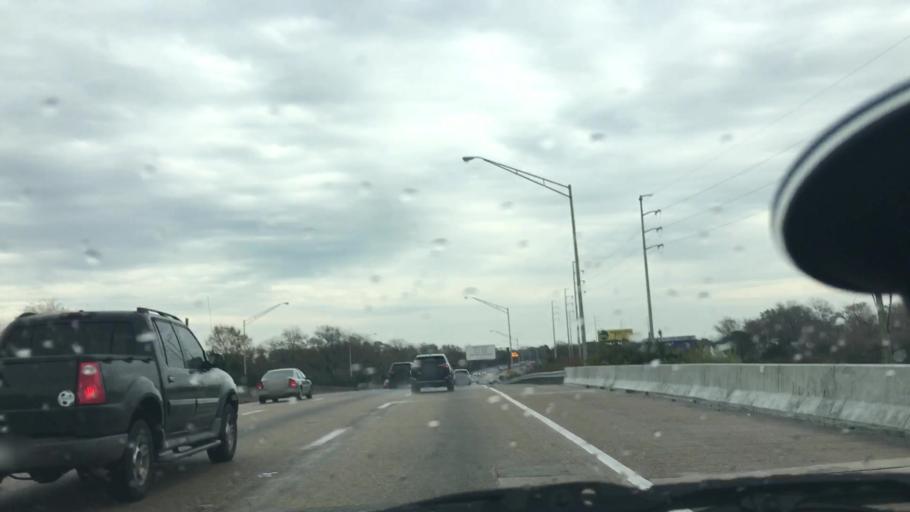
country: US
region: Virginia
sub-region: City of Hampton
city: Hampton
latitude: 37.0341
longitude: -76.3468
